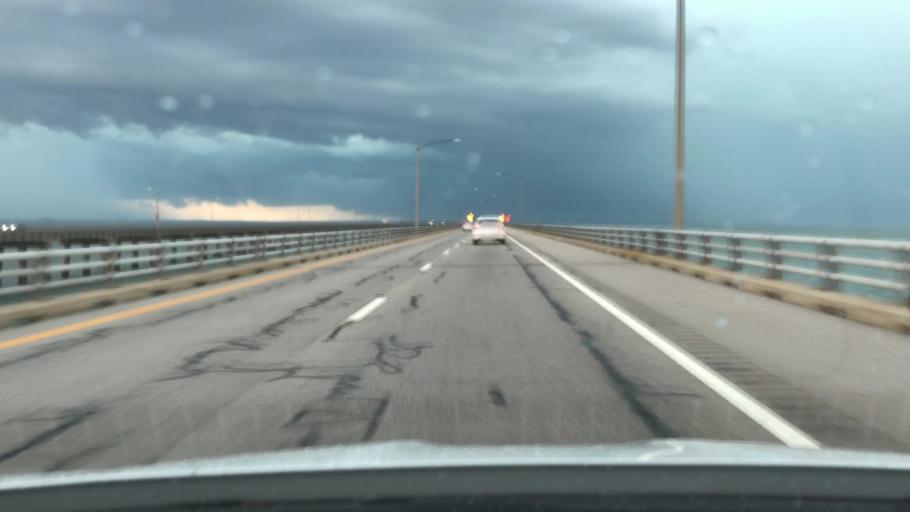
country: US
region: Virginia
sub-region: City of Virginia Beach
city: Virginia Beach
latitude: 37.0028
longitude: -76.0984
